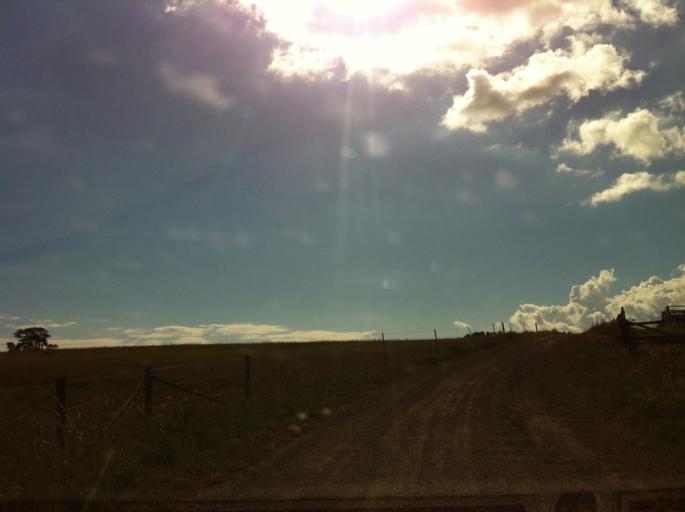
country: SE
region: Skane
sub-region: Ystads Kommun
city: Kopingebro
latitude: 55.3920
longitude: 14.0475
